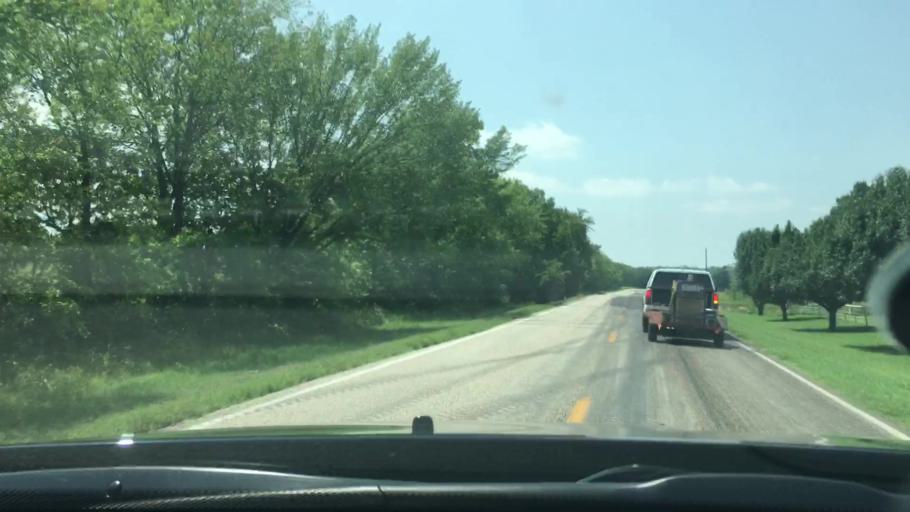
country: US
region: Oklahoma
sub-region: Johnston County
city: Tishomingo
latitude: 34.3749
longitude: -96.4409
